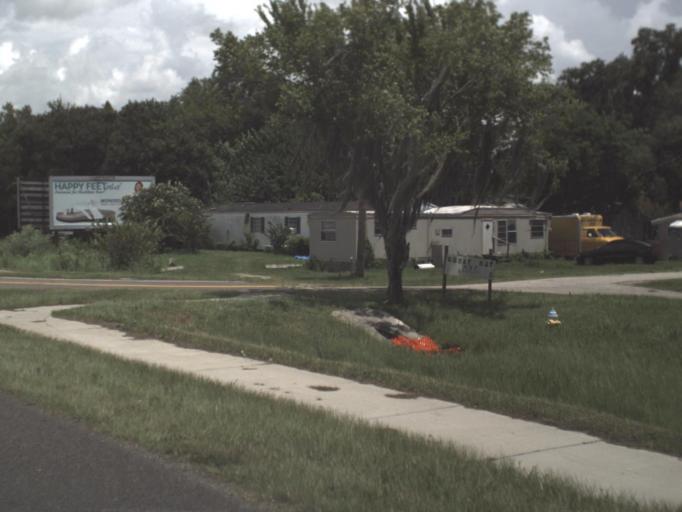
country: US
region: Florida
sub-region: Hillsborough County
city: East Lake-Orient Park
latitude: 28.0076
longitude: -82.3554
